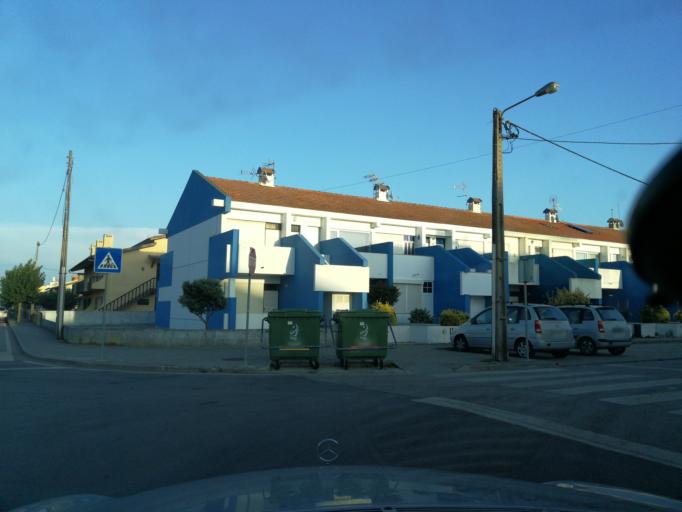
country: PT
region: Aveiro
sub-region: Murtosa
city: Murtosa
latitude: 40.7592
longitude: -8.7099
